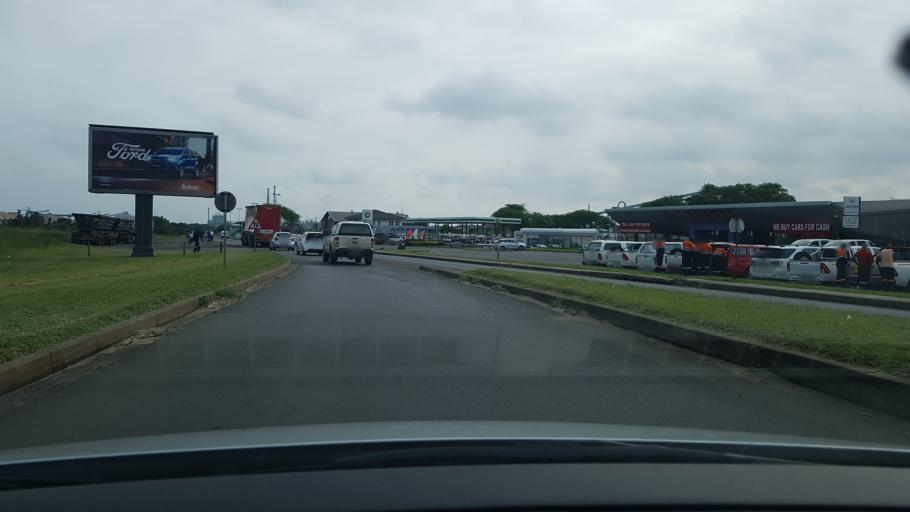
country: ZA
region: KwaZulu-Natal
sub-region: uThungulu District Municipality
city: Richards Bay
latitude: -28.7583
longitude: 32.0445
